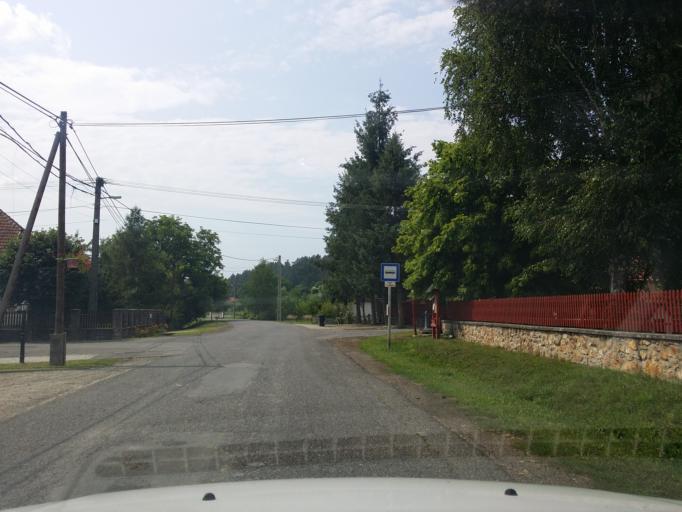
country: HU
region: Borsod-Abauj-Zemplen
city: Sarospatak
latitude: 48.4555
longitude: 21.5287
